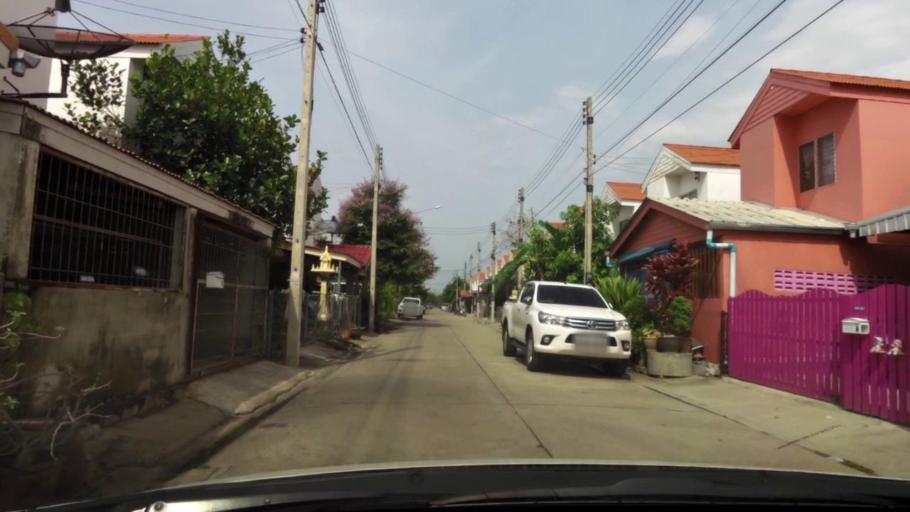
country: TH
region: Ratchaburi
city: Ratchaburi
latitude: 13.5377
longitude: 99.7906
